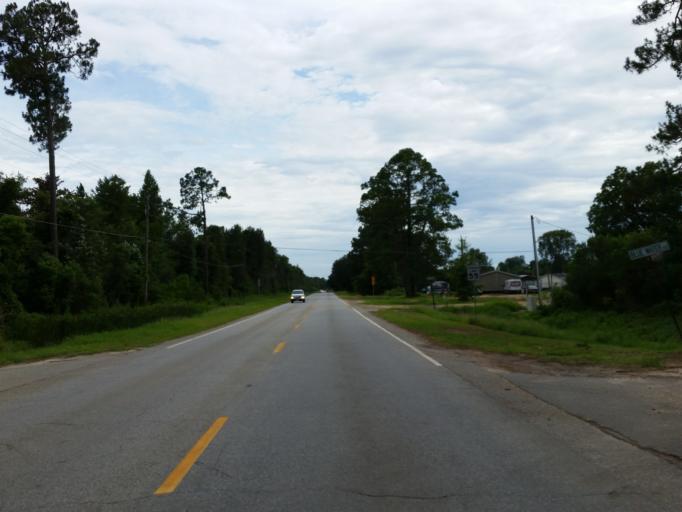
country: US
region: Georgia
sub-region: Lowndes County
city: Valdosta
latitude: 30.7416
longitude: -83.2784
